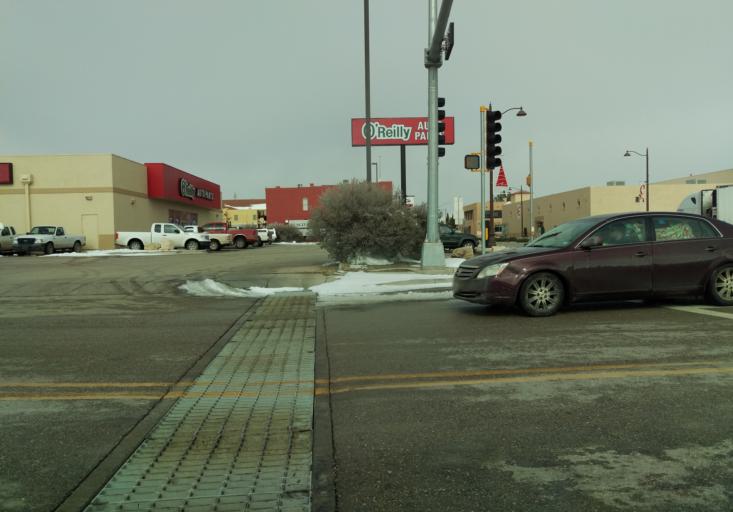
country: US
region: New Mexico
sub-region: Eddy County
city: Carlsbad
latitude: 32.4179
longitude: -104.2292
